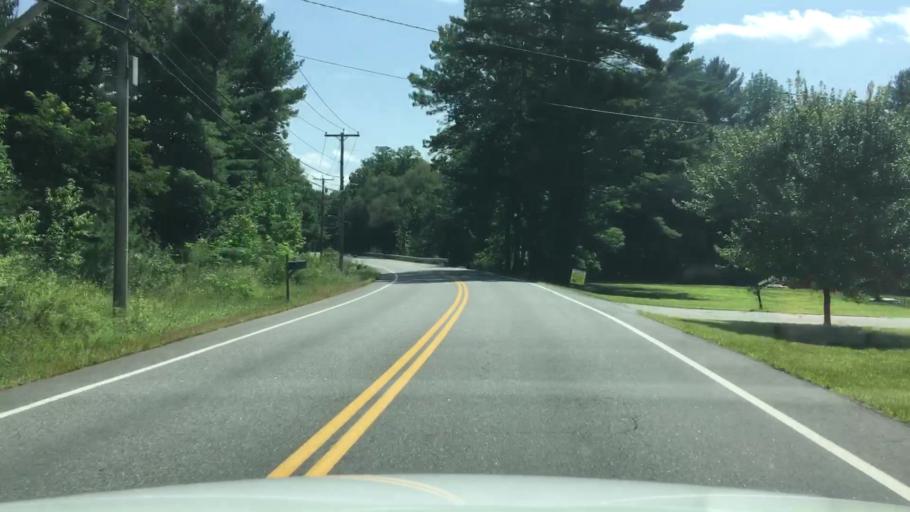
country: US
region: Maine
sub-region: Kennebec County
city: Augusta
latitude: 44.3374
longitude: -69.8071
